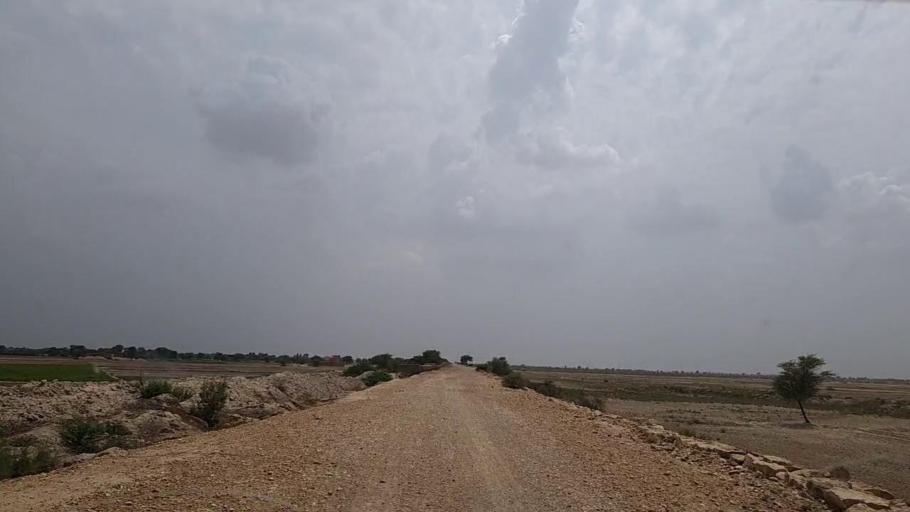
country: PK
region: Sindh
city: Johi
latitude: 26.7398
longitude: 67.5843
